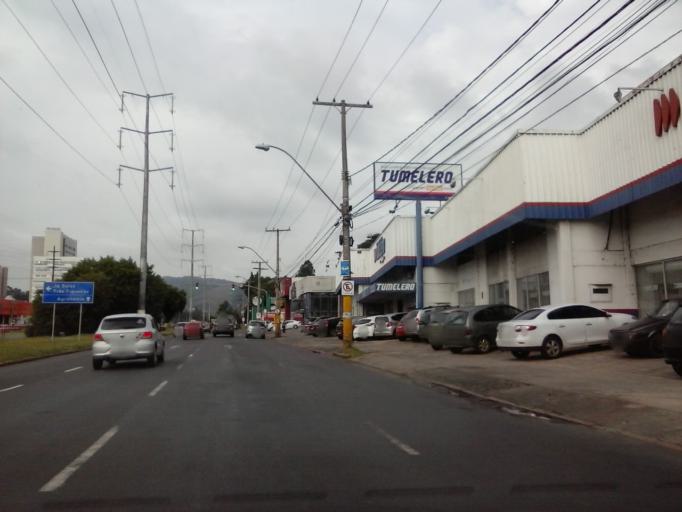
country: BR
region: Rio Grande do Sul
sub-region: Porto Alegre
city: Porto Alegre
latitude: -30.0560
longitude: -51.1681
